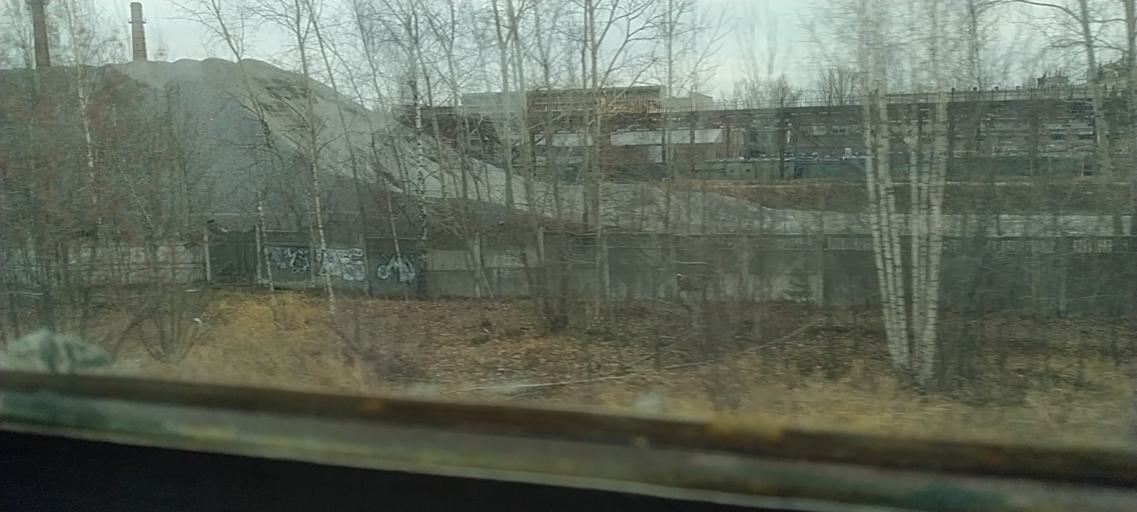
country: RU
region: Moskovskaya
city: Kraskovo
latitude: 55.6692
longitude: 37.9800
